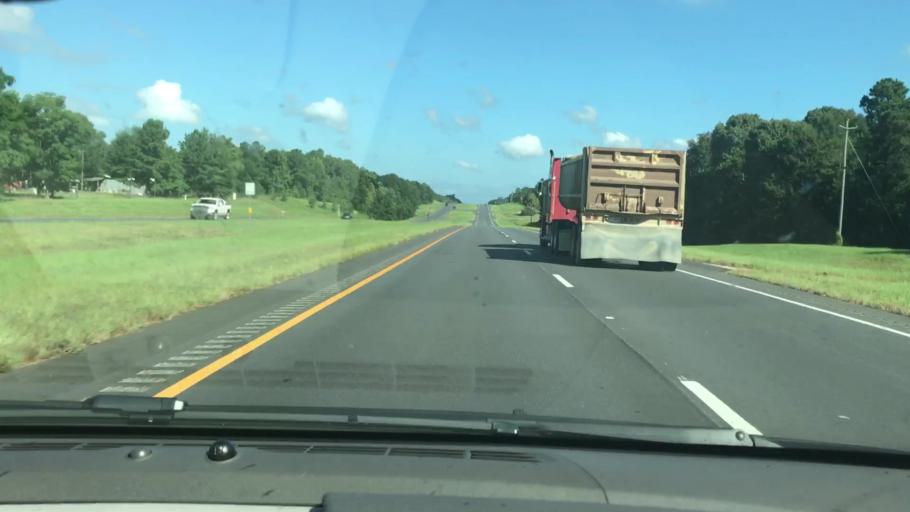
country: US
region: Alabama
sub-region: Barbour County
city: Eufaula
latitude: 32.0317
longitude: -85.1225
